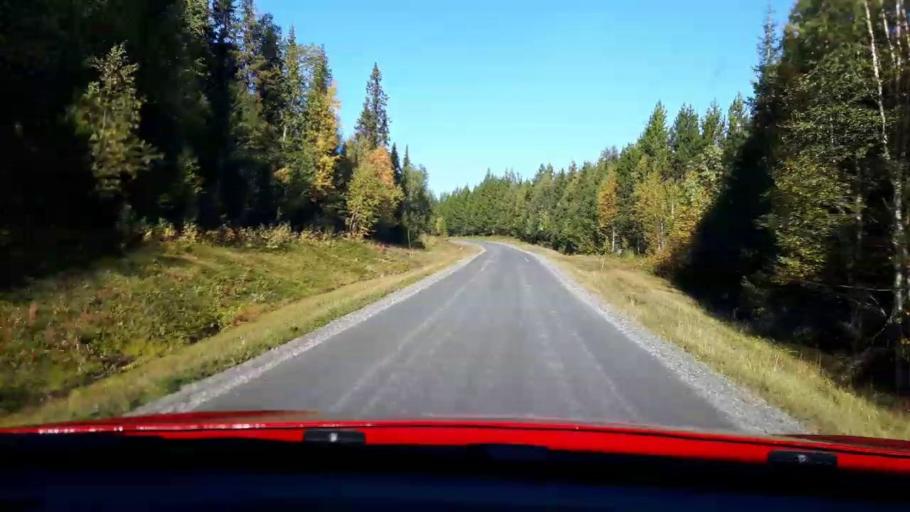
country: NO
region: Nord-Trondelag
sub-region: Lierne
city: Sandvika
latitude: 64.5323
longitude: 14.0364
